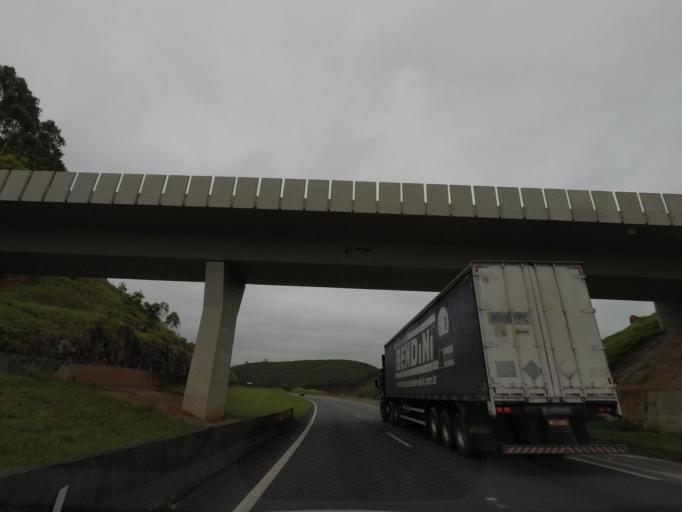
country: BR
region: Sao Paulo
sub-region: Jacarei
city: Jacarei
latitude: -23.2592
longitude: -46.0956
